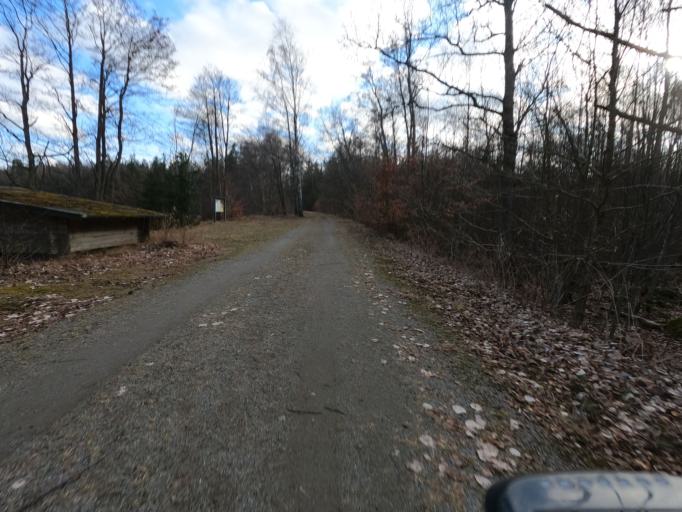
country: SE
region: Kronoberg
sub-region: Vaxjo Kommun
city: Gemla
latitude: 56.6607
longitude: 14.6197
